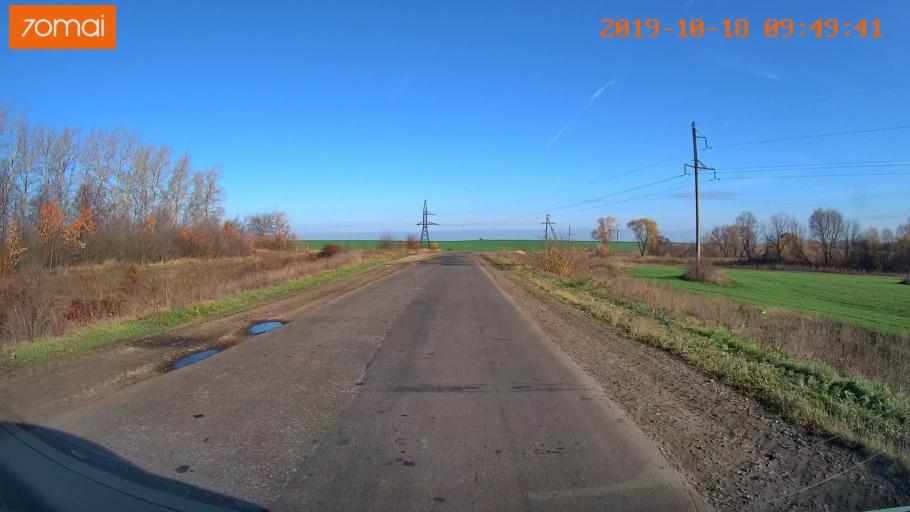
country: RU
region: Tula
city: Kazachka
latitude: 53.3207
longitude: 38.2687
